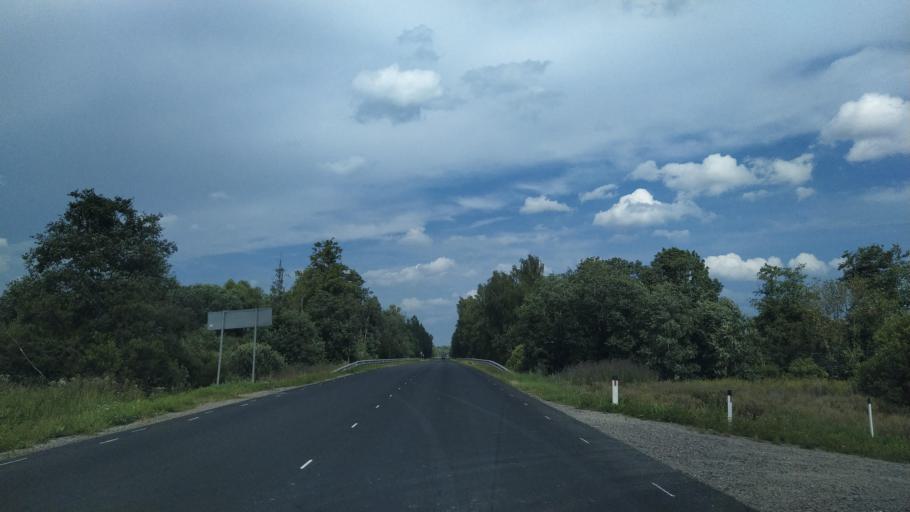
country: RU
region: Pskov
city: Vybor
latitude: 57.7192
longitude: 28.9478
